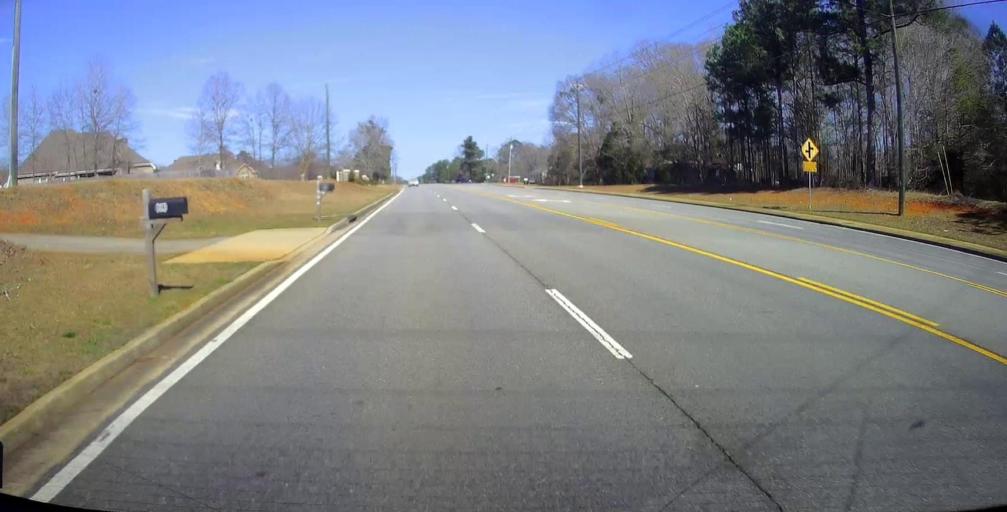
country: US
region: Georgia
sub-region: Houston County
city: Robins Air Force Base
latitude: 32.5264
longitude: -83.6365
